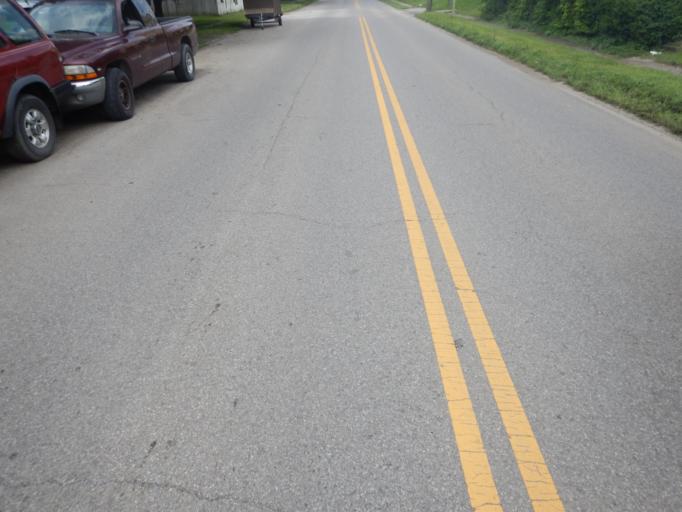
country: US
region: Ohio
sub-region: Muskingum County
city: Zanesville
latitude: 39.9306
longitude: -82.0254
